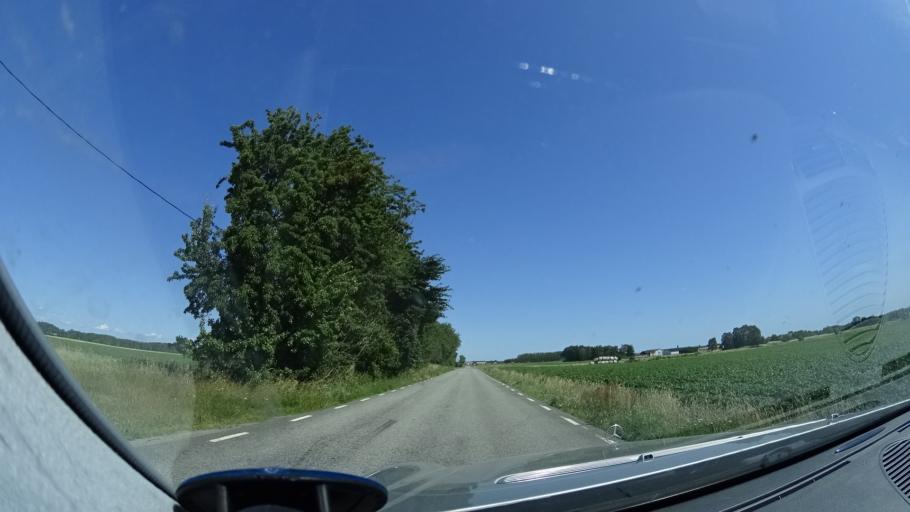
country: SE
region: Skane
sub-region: Kristianstads Kommun
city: Degeberga
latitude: 55.8868
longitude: 14.0274
